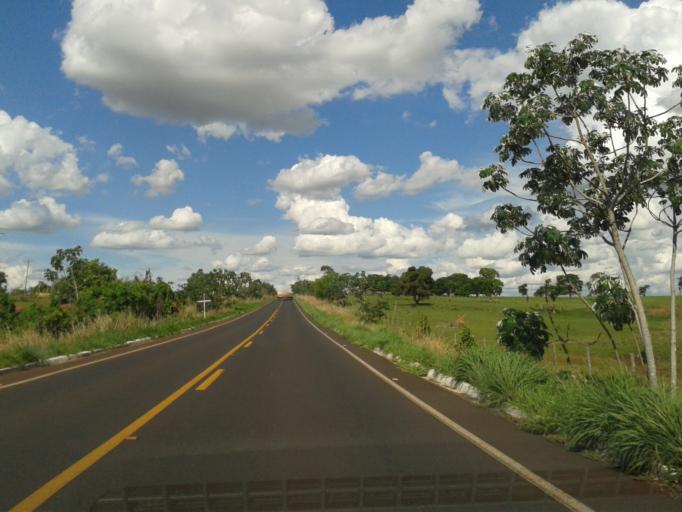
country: BR
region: Minas Gerais
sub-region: Iturama
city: Iturama
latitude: -19.6231
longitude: -50.0821
